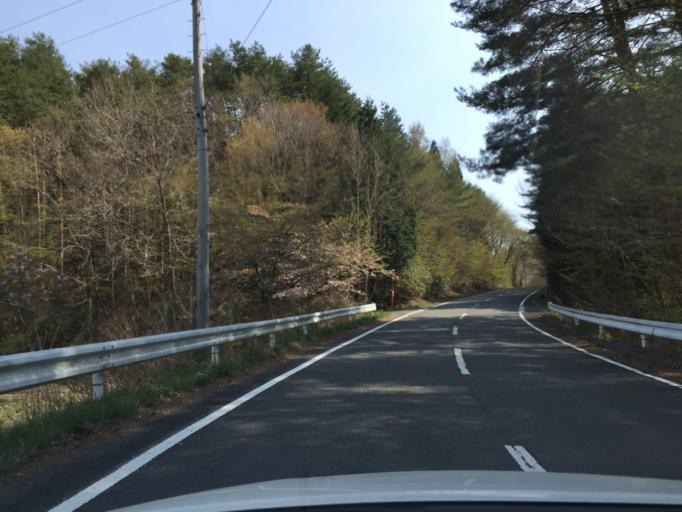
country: JP
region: Fukushima
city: Iwaki
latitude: 37.2427
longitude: 140.8461
